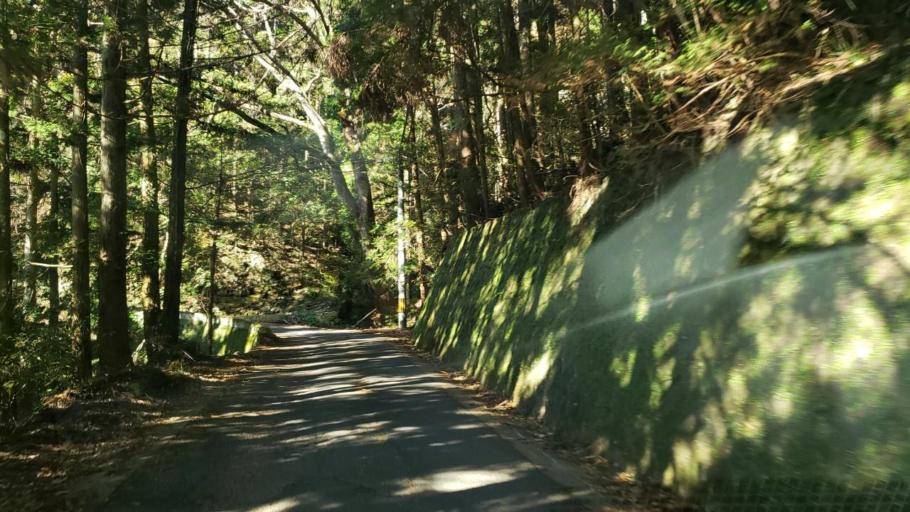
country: JP
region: Tokushima
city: Wakimachi
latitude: 33.9905
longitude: 134.0023
